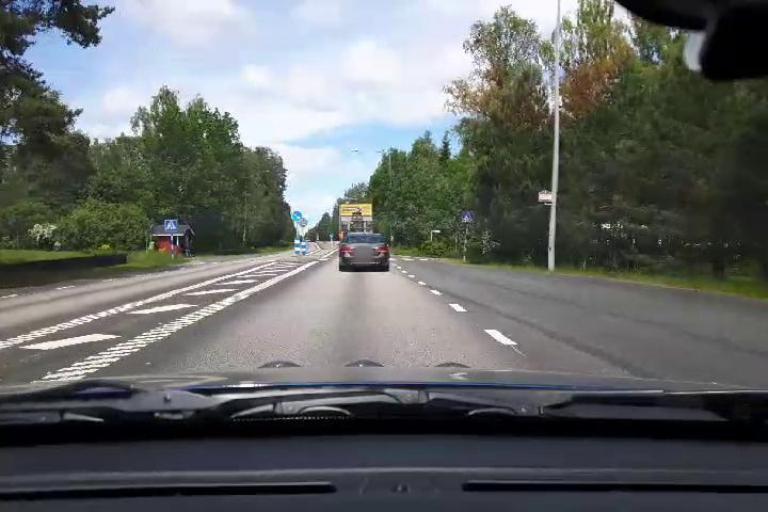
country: SE
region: Uppsala
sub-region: Osthammars Kommun
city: Bjorklinge
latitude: 60.0394
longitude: 17.5506
